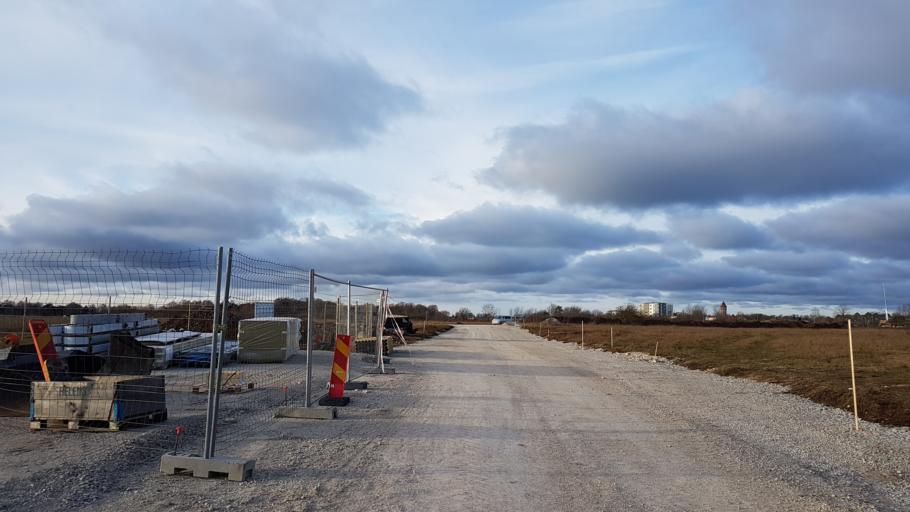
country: SE
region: Gotland
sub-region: Gotland
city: Visby
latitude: 57.6243
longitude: 18.3161
